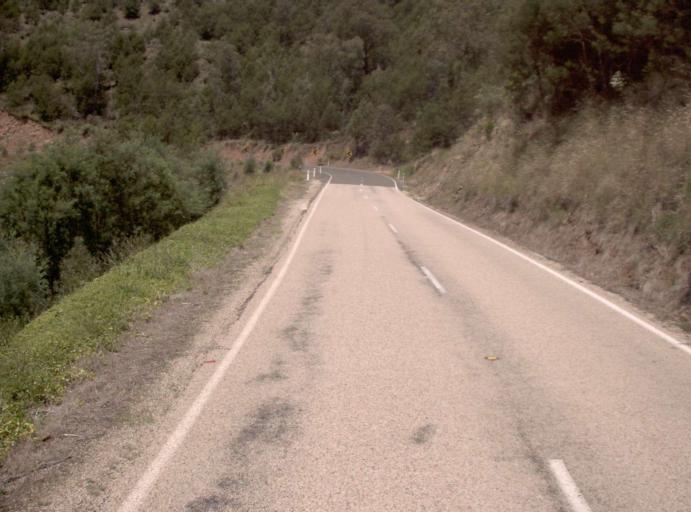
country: AU
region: Victoria
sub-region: East Gippsland
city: Bairnsdale
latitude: -37.5279
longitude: 147.8432
